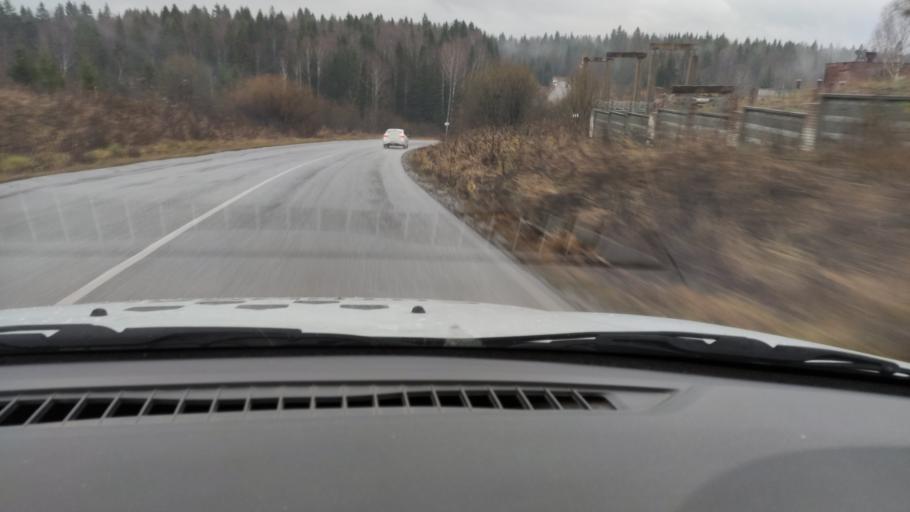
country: RU
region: Perm
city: Novyye Lyady
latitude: 58.0409
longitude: 56.5985
